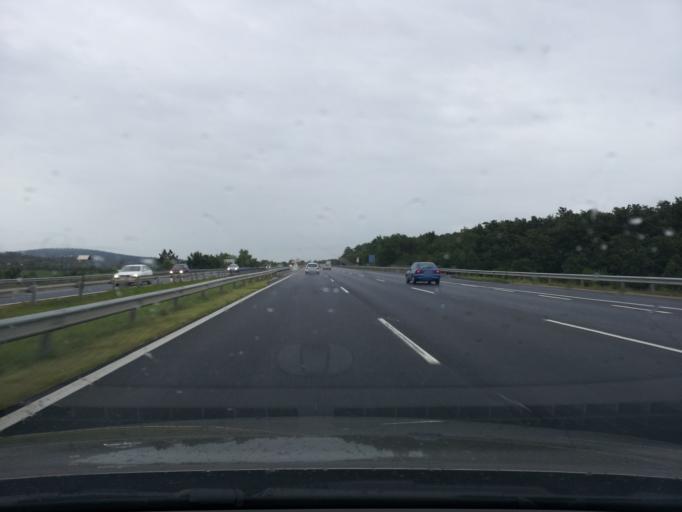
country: HU
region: Fejer
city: Pakozd
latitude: 47.2266
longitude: 18.5735
